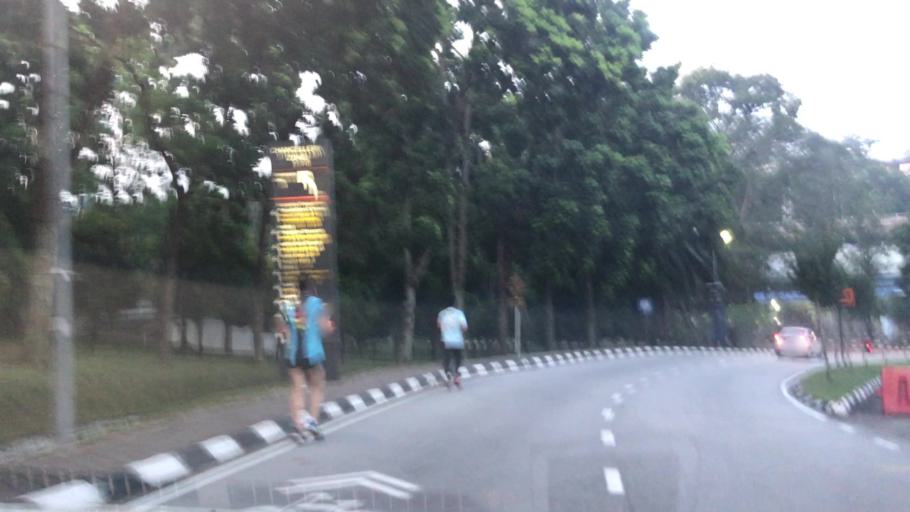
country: MY
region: Kuala Lumpur
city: Kuala Lumpur
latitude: 3.1218
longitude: 101.6597
